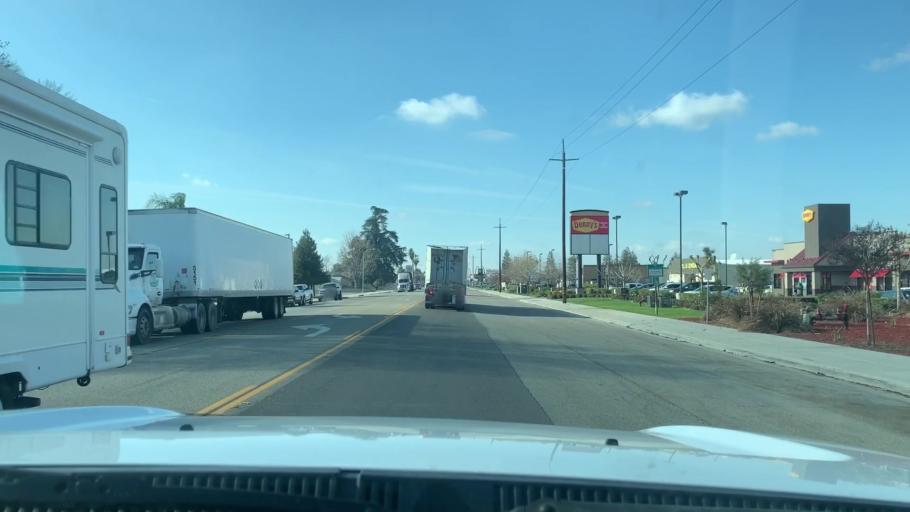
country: US
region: California
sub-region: Kern County
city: Wasco
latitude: 35.6016
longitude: -119.3453
